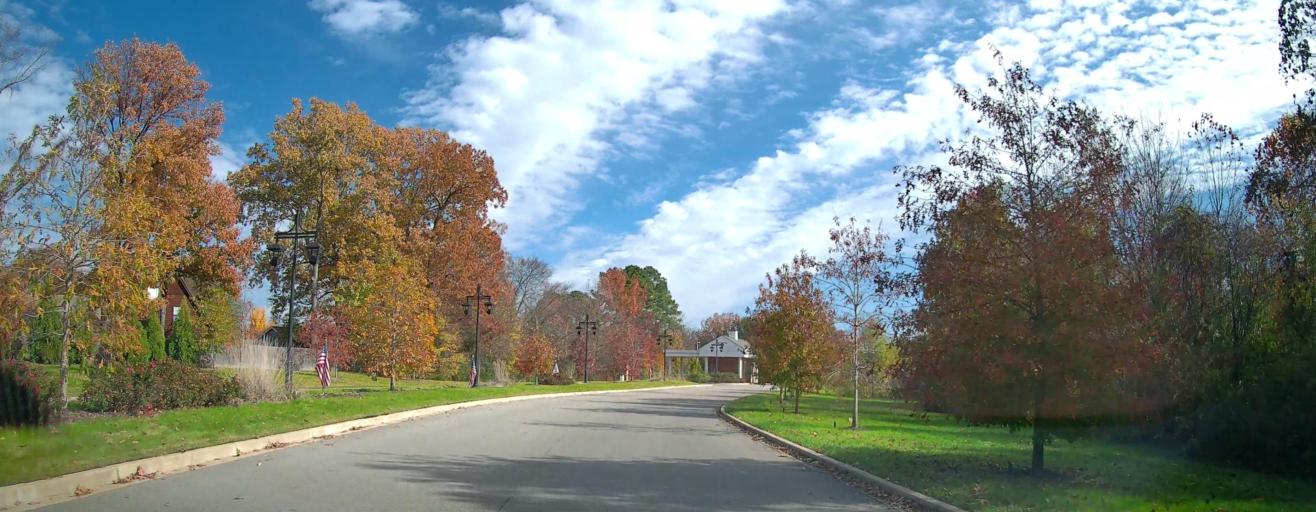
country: US
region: Tennessee
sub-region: Shelby County
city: Germantown
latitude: 35.0522
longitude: -89.8460
